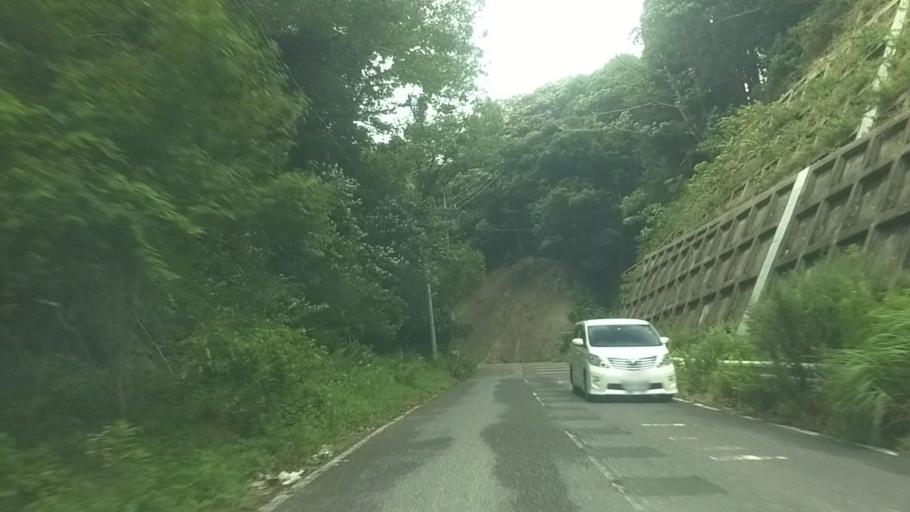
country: JP
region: Chiba
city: Kawaguchi
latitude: 35.2292
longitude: 140.0294
